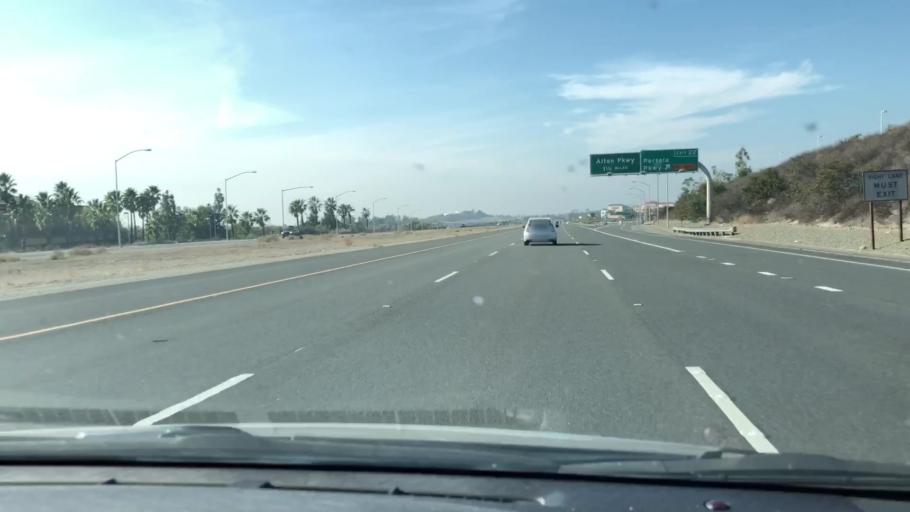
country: US
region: California
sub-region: Orange County
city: Portola Hills
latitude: 33.6652
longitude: -117.6437
